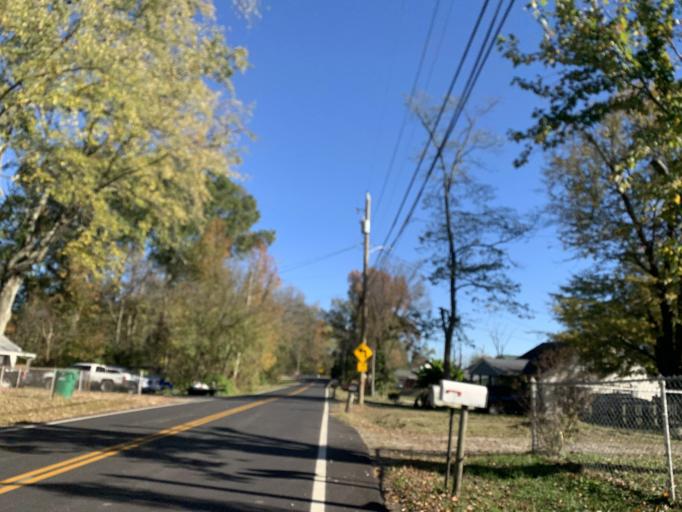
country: US
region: Kentucky
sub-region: Jefferson County
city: Pleasure Ridge Park
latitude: 38.1563
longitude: -85.8717
